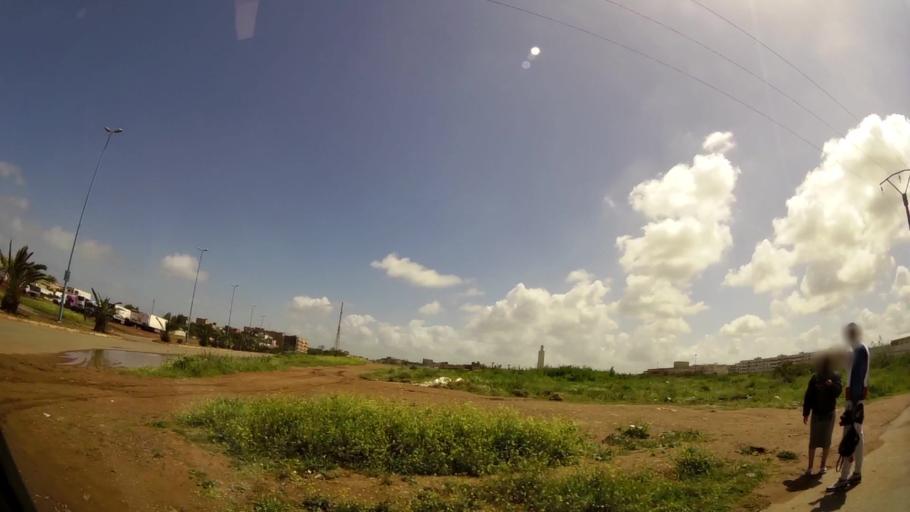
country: MA
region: Grand Casablanca
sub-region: Mediouna
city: Tit Mellil
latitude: 33.6359
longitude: -7.4596
